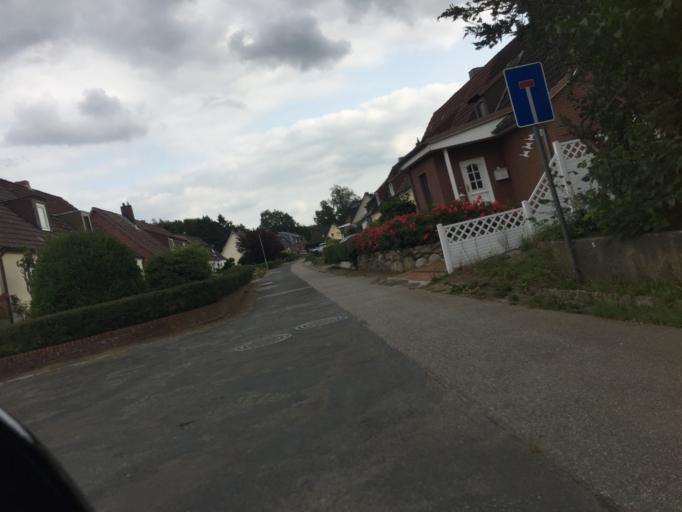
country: DE
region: Schleswig-Holstein
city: Itzehoe
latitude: 53.9443
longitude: 9.5187
